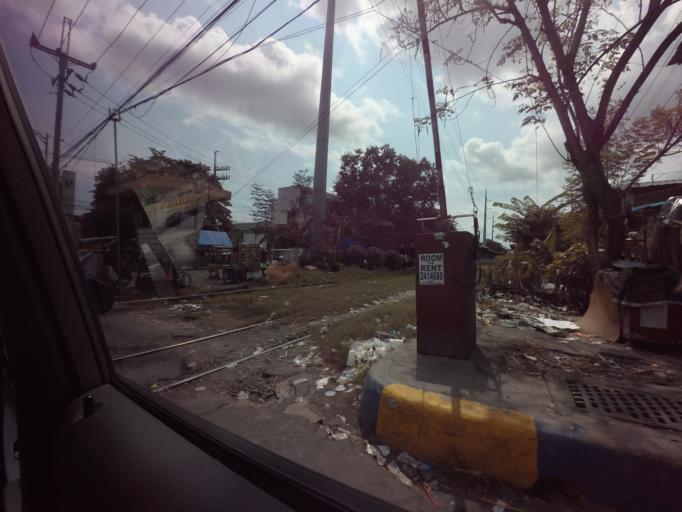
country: PH
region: Metro Manila
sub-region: San Juan
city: San Juan
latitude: 14.5995
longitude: 121.0121
